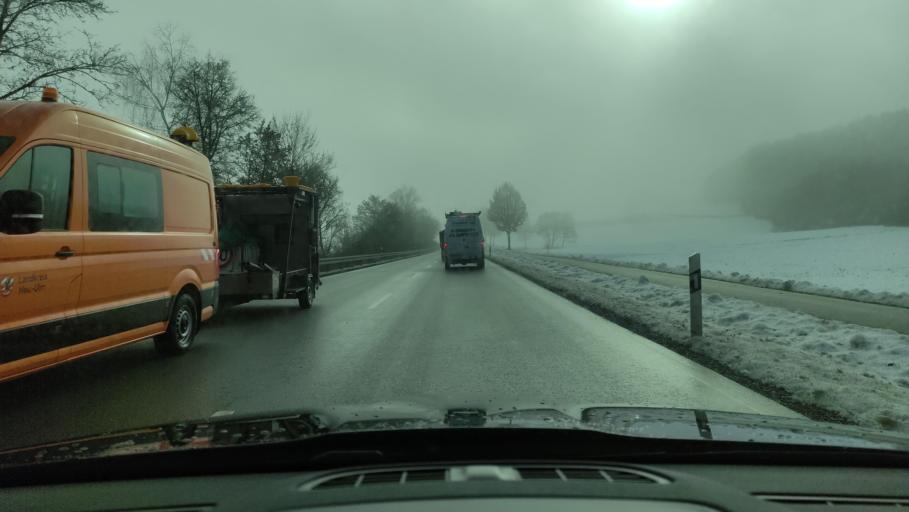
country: DE
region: Bavaria
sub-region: Swabia
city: Krumbach
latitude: 48.2610
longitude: 10.3500
